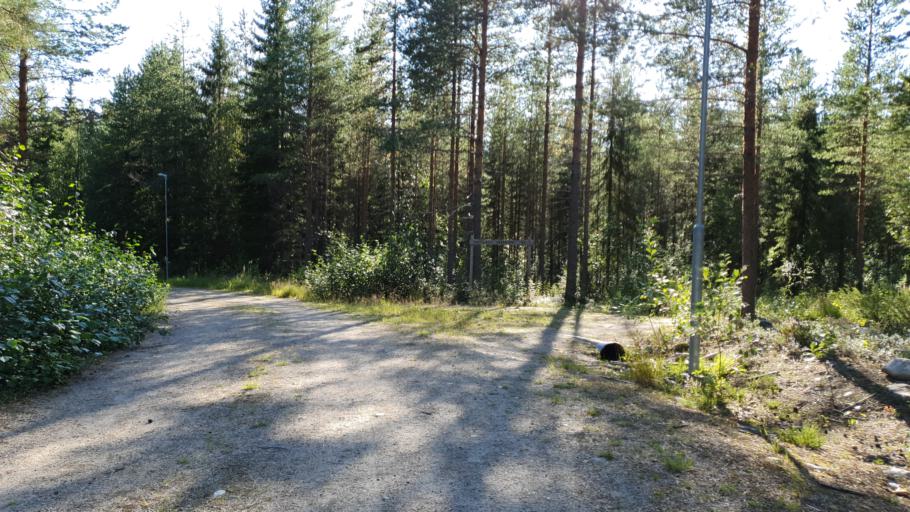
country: FI
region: Kainuu
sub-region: Kehys-Kainuu
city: Kuhmo
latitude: 64.1137
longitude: 29.5004
